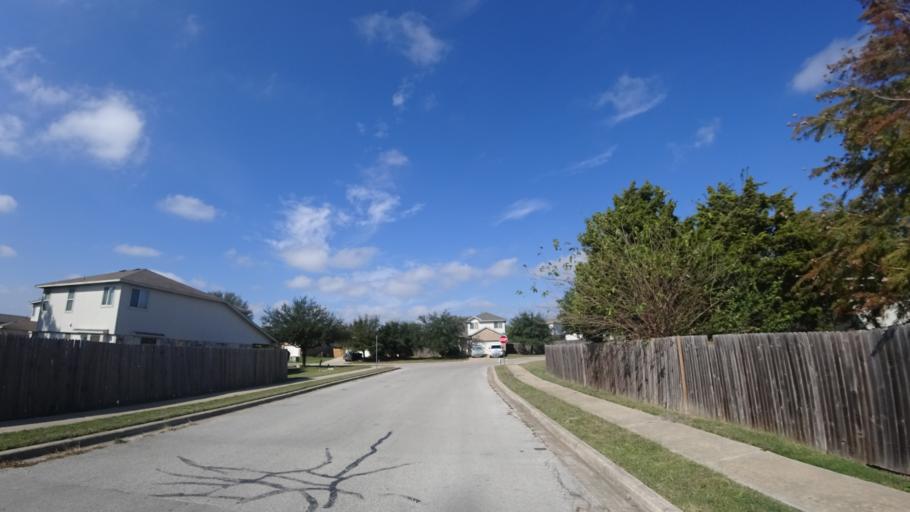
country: US
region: Texas
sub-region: Travis County
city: Pflugerville
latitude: 30.4209
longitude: -97.6371
